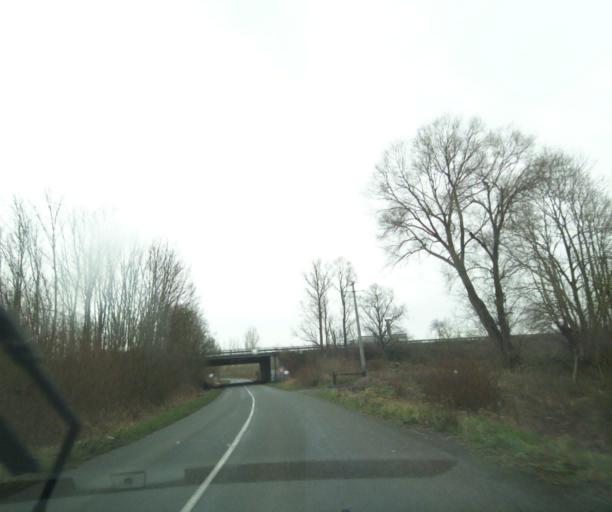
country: FR
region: Nord-Pas-de-Calais
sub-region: Departement du Nord
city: Crespin
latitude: 50.4319
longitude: 3.6503
